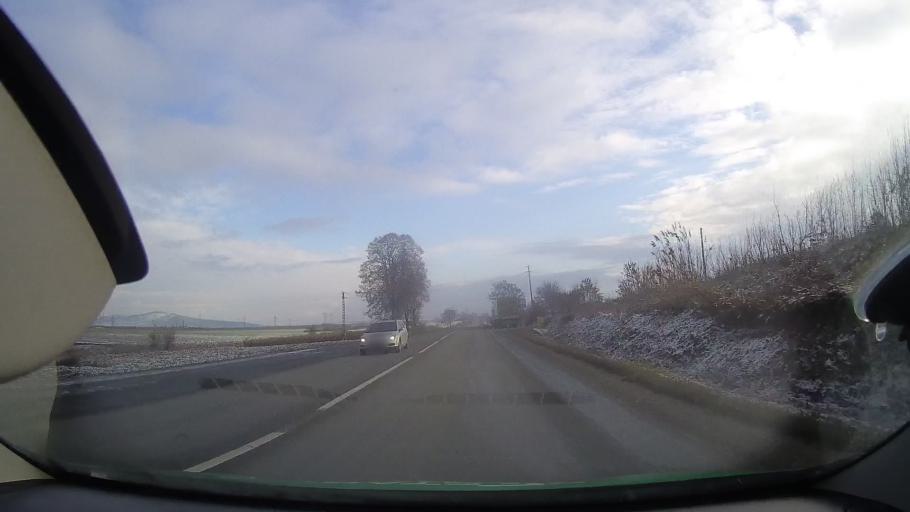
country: RO
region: Mures
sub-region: Comuna Cuci
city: Cuci
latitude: 46.4595
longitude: 24.1679
